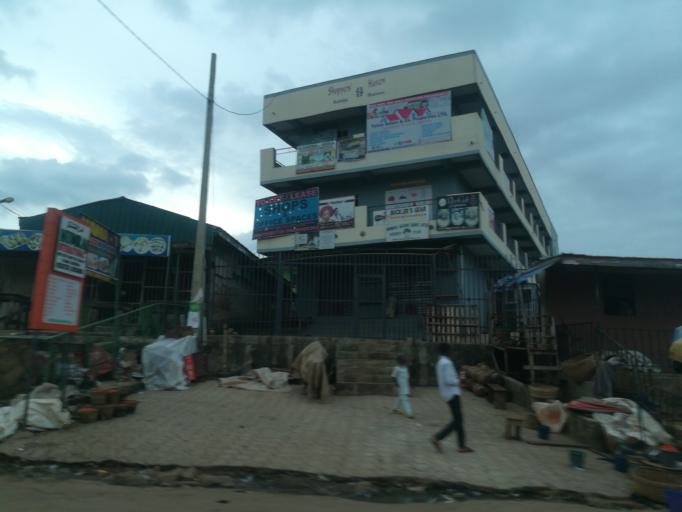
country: NG
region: Oyo
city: Ibadan
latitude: 7.4354
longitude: 3.9104
